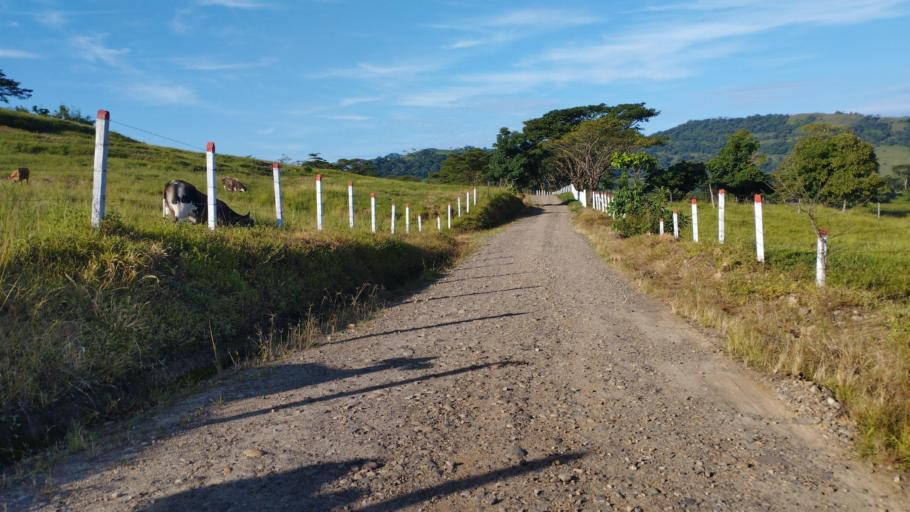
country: CO
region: Boyaca
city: San Luis de Gaceno
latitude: 4.7925
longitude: -73.0959
